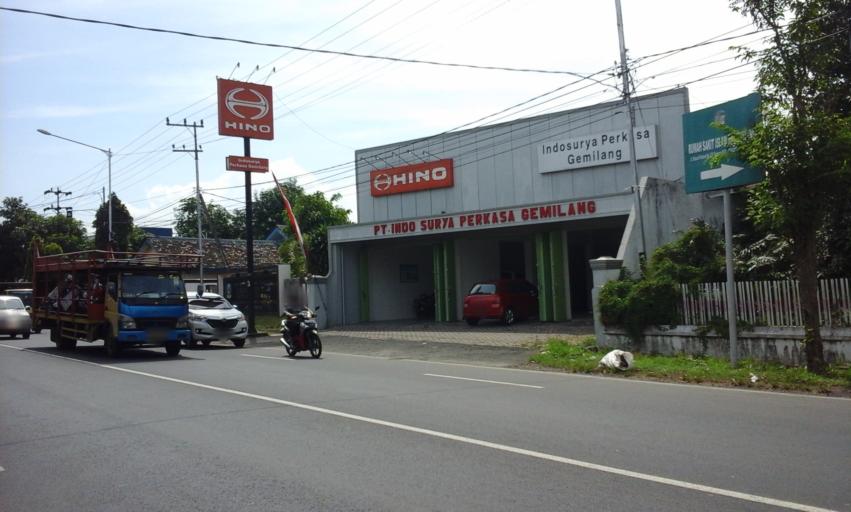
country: ID
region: East Java
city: Krajan
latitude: -8.2454
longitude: 114.3507
